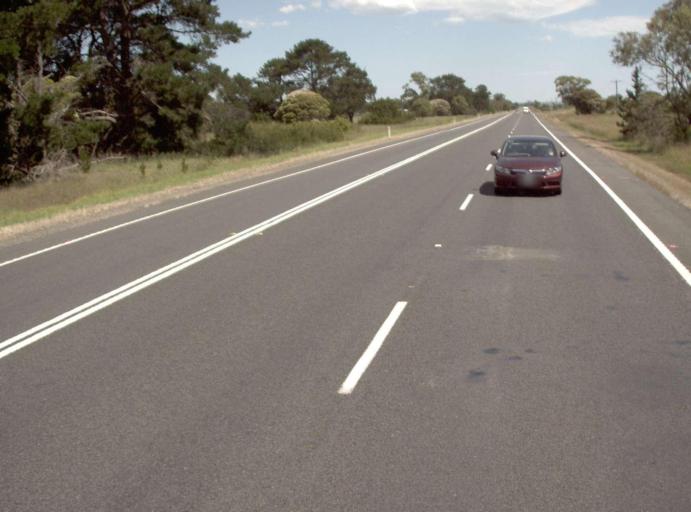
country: AU
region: Victoria
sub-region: Wellington
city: Sale
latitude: -38.0175
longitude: 147.0607
